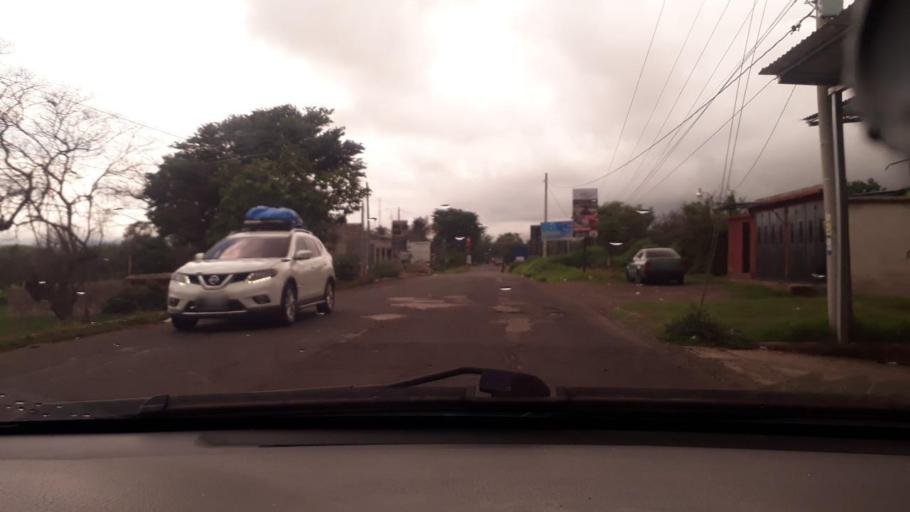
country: GT
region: Jutiapa
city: Jalpatagua
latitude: 14.1389
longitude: -90.0168
